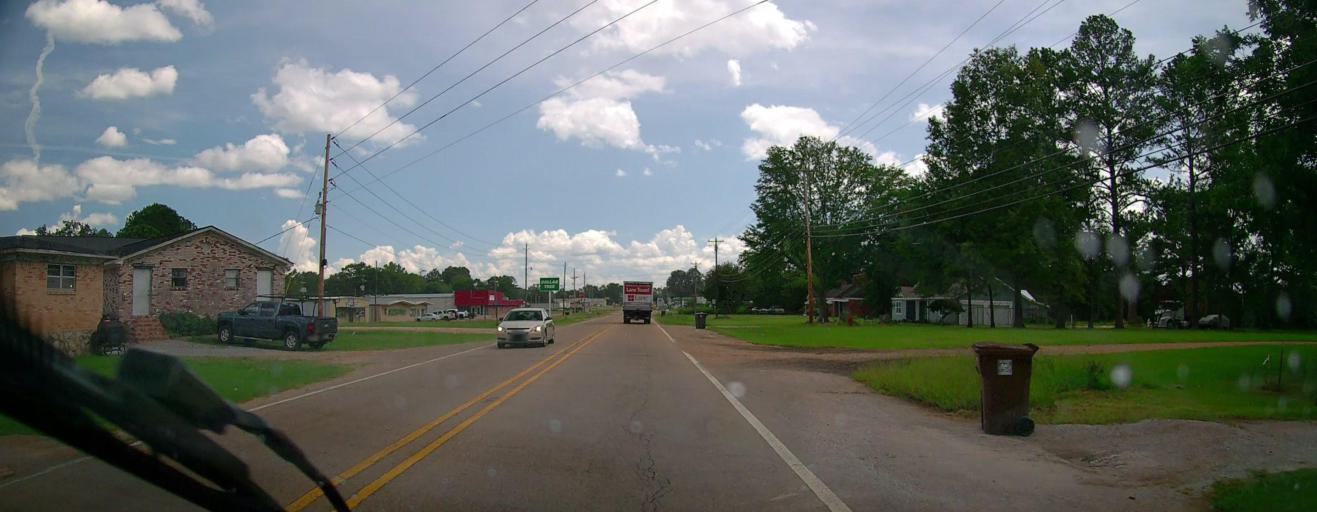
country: US
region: Mississippi
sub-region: Lee County
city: Shannon
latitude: 34.1304
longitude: -88.7193
